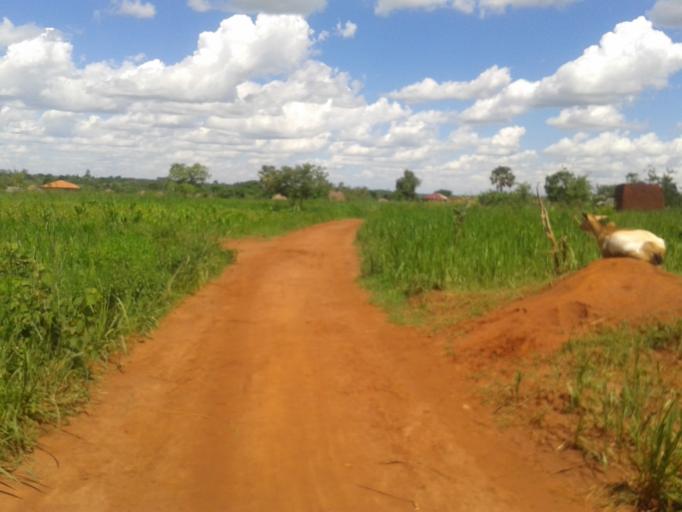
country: UG
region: Northern Region
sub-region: Gulu District
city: Gulu
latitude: 2.7575
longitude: 32.3283
